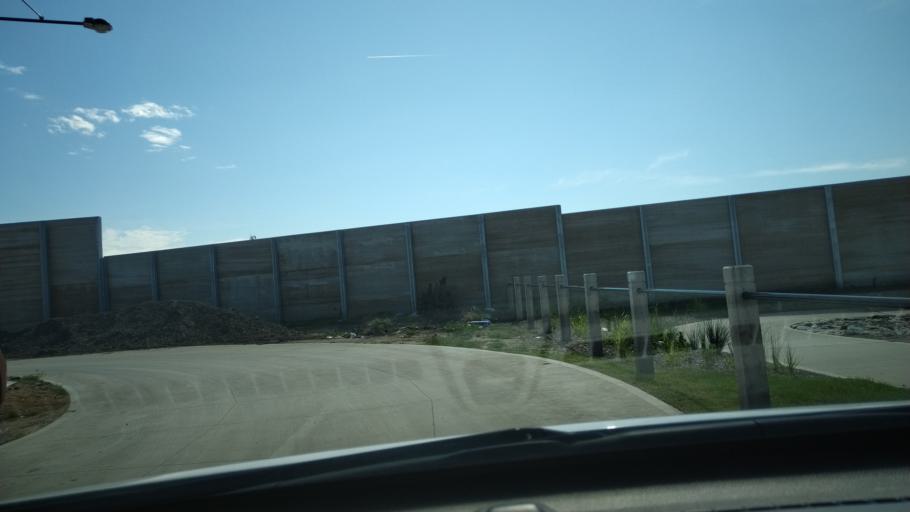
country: AU
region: Victoria
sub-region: Greater Dandenong
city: Keysborough
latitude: -37.9990
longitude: 145.1710
